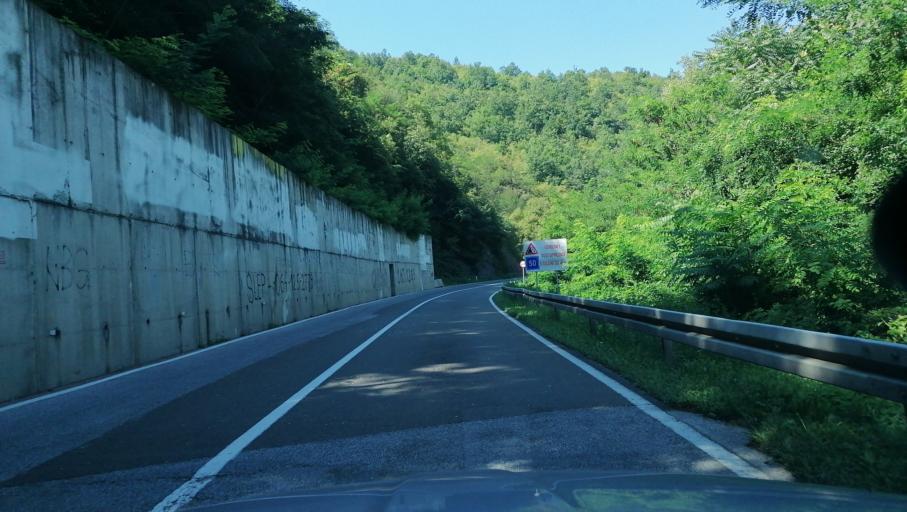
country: RS
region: Central Serbia
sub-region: Raski Okrug
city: Kraljevo
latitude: 43.6130
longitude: 20.5470
